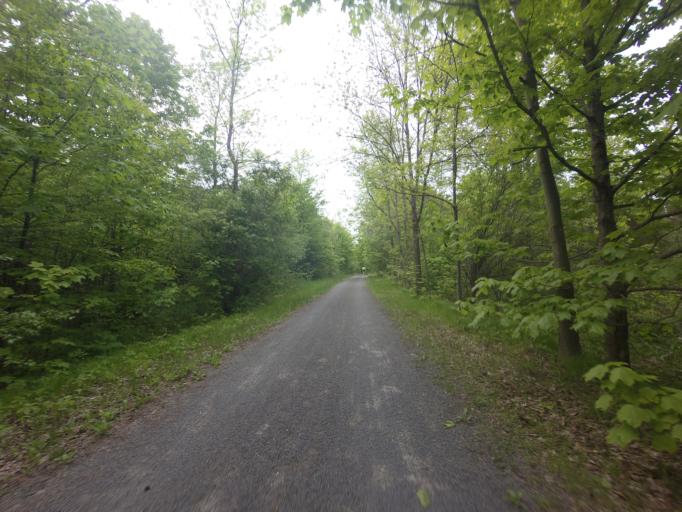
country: CA
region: Ontario
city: Kingston
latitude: 44.3349
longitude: -76.5901
